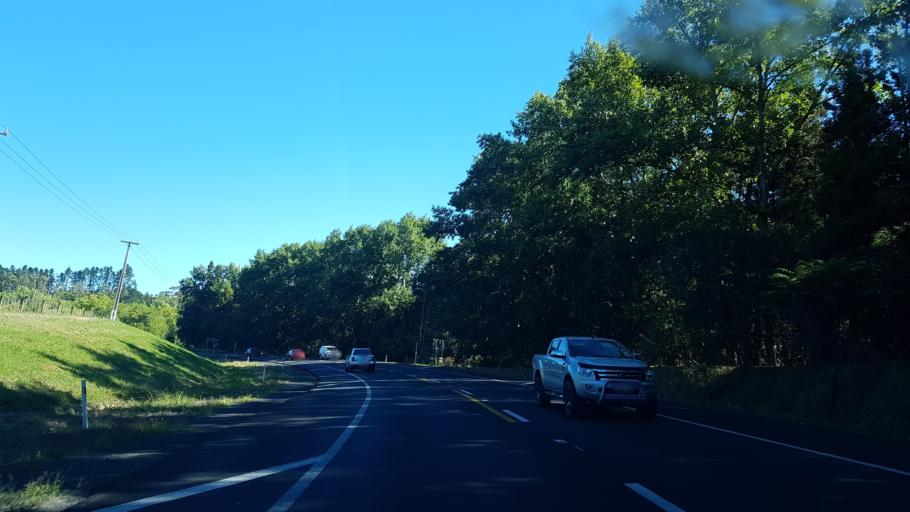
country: NZ
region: Auckland
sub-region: Auckland
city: Warkworth
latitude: -36.4354
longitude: 174.6484
